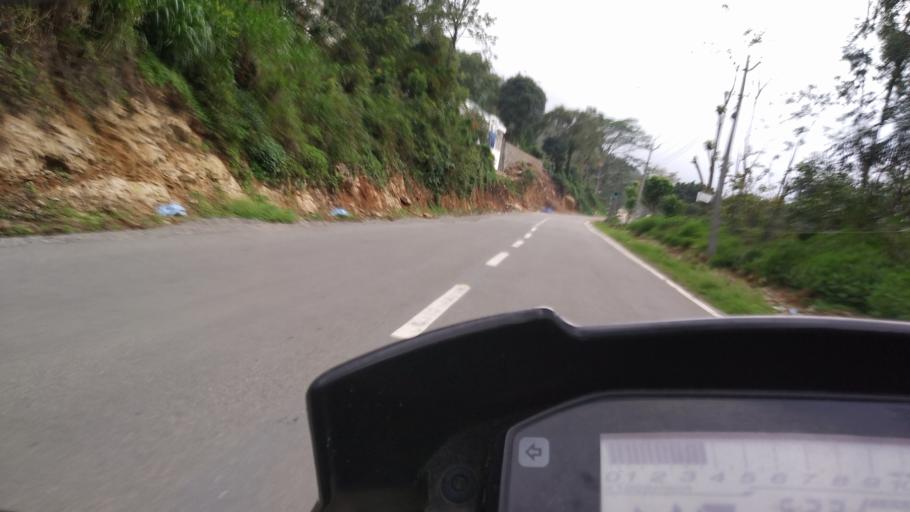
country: IN
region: Tamil Nadu
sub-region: Theni
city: Bodinayakkanur
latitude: 10.0104
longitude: 77.2358
